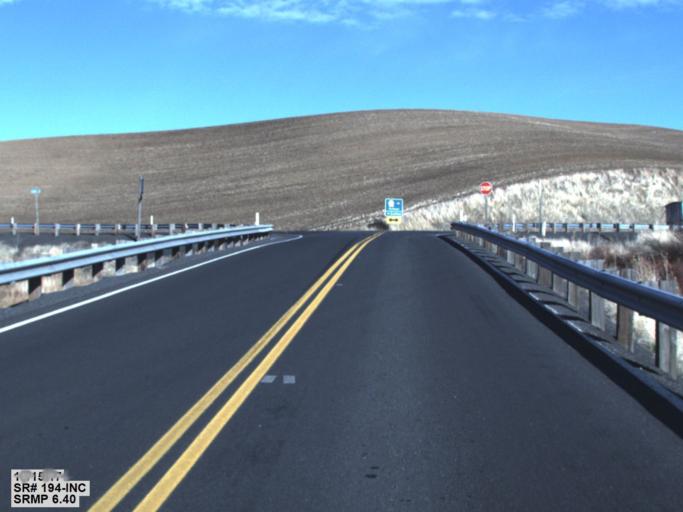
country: US
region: Washington
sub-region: Whitman County
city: Colfax
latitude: 46.7552
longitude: -117.4571
